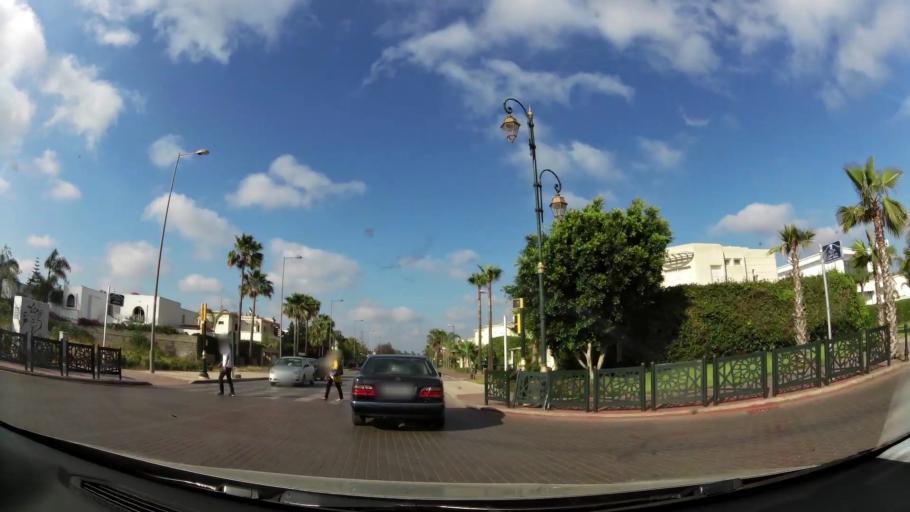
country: MA
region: Rabat-Sale-Zemmour-Zaer
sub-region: Skhirate-Temara
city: Temara
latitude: 33.9520
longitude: -6.8620
